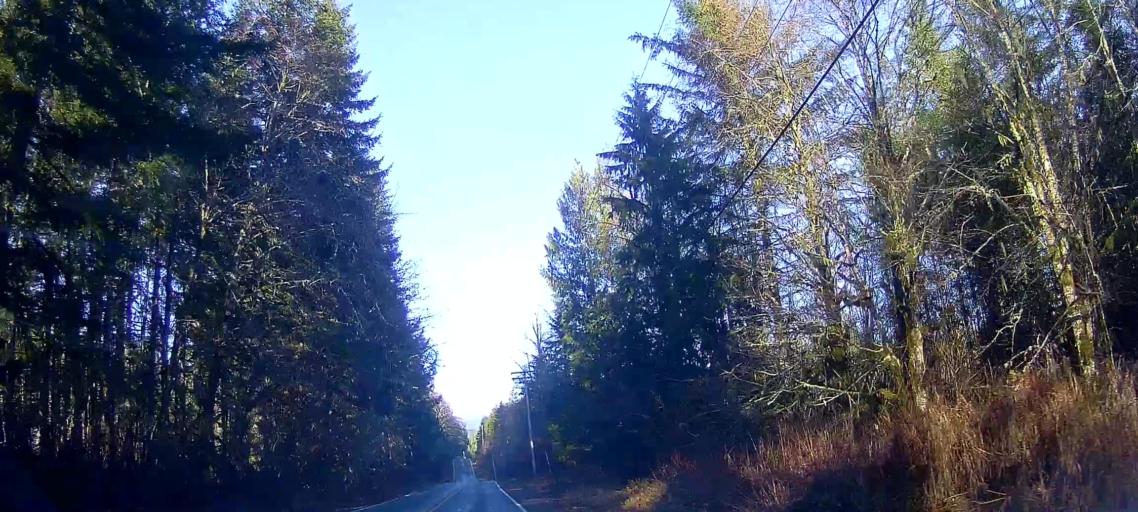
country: US
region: Washington
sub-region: Snohomish County
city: Darrington
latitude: 48.5586
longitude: -121.7658
